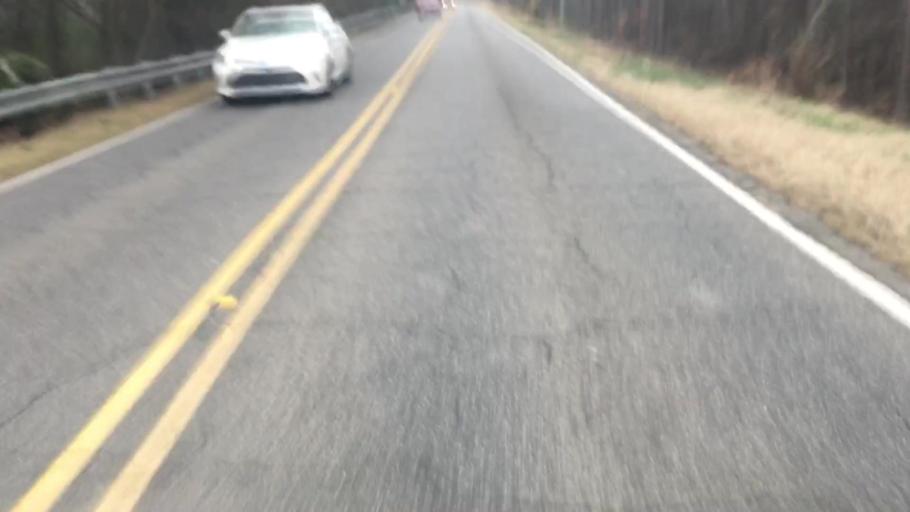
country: US
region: Alabama
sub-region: Jefferson County
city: Cahaba Heights
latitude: 33.4422
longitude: -86.7395
